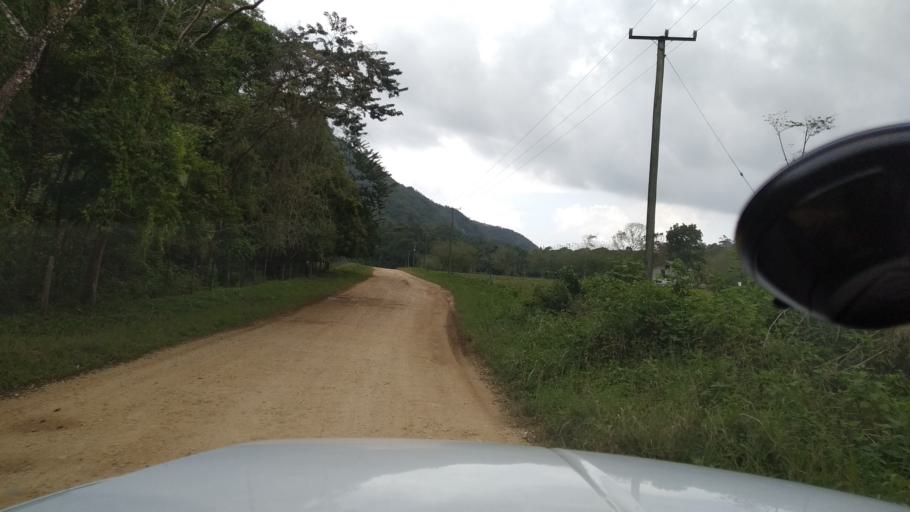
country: BZ
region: Toledo
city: Punta Gorda
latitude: 16.2089
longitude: -89.0247
